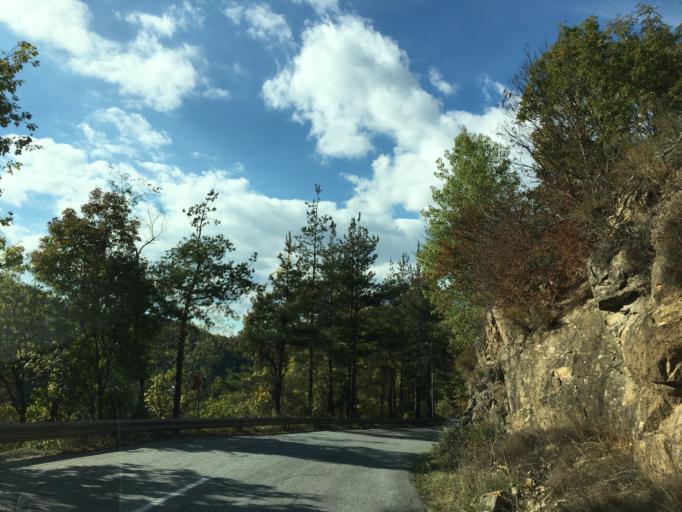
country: BG
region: Smolyan
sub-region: Obshtina Madan
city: Madan
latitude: 41.4566
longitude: 24.9767
